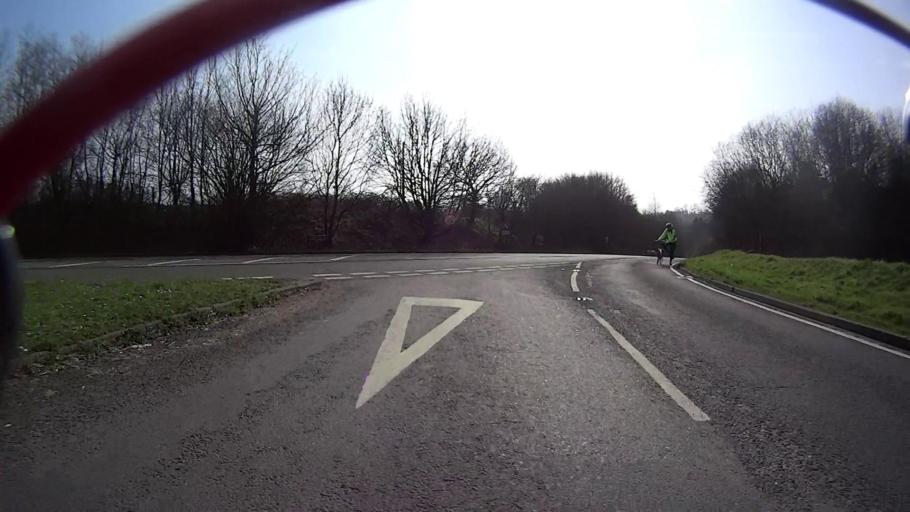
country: GB
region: England
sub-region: Surrey
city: Headley
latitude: 51.2634
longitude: -0.2622
